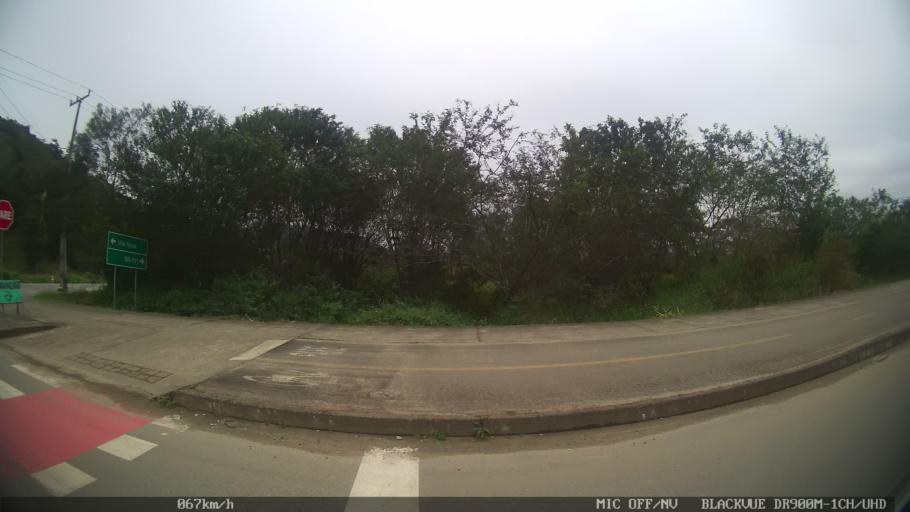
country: BR
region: Santa Catarina
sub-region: Joinville
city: Joinville
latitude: -26.2781
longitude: -48.9235
